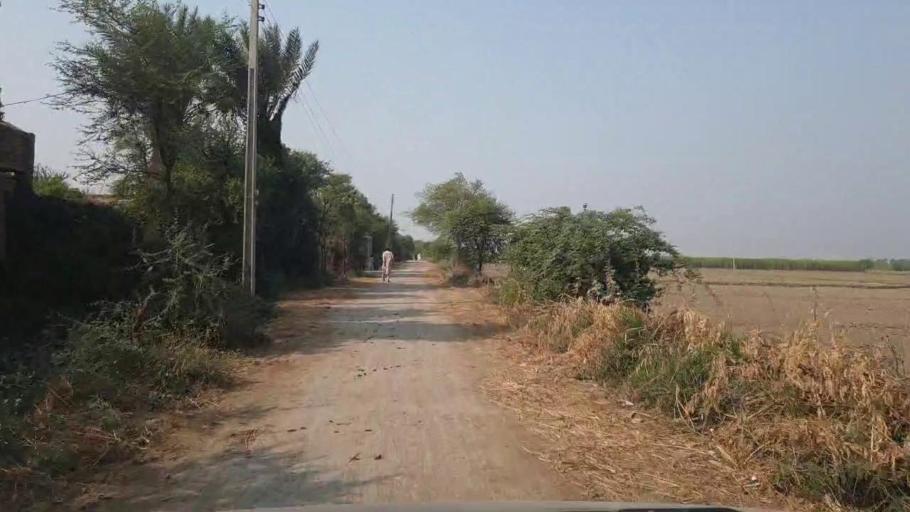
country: PK
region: Sindh
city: Tando Muhammad Khan
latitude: 25.0550
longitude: 68.3659
